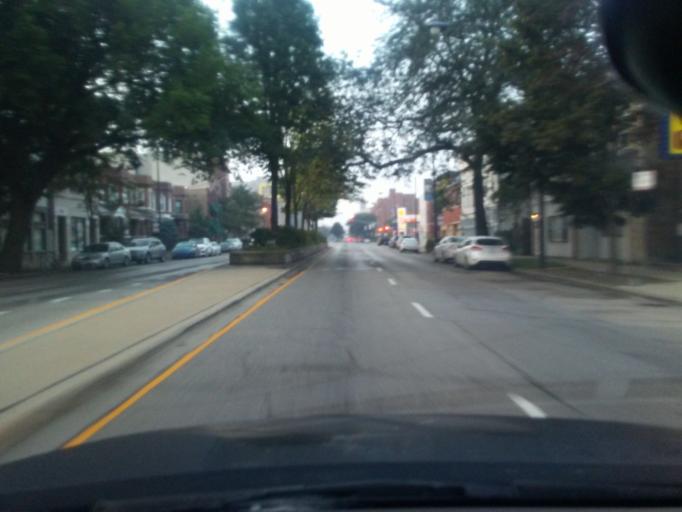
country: US
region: Illinois
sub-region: Cook County
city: Lincolnwood
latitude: 41.9483
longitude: -87.6690
